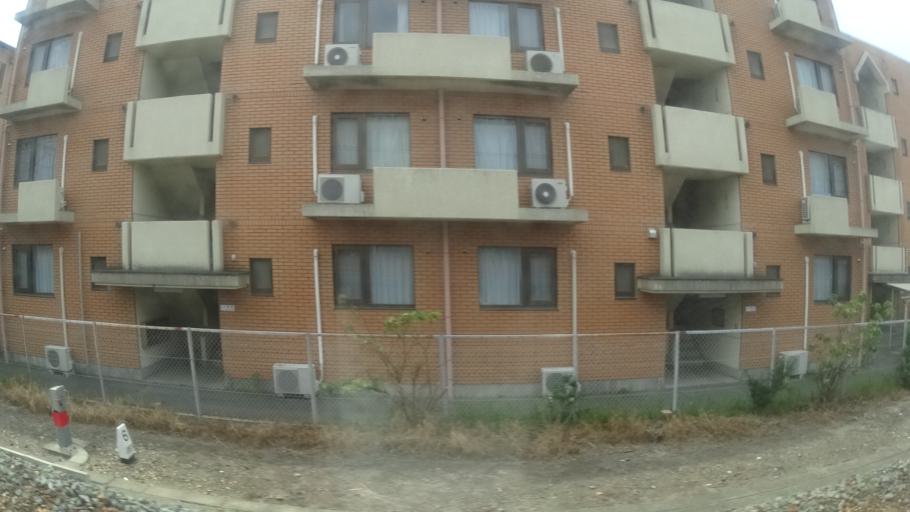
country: JP
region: Shizuoka
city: Hamamatsu
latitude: 34.6904
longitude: 137.6898
